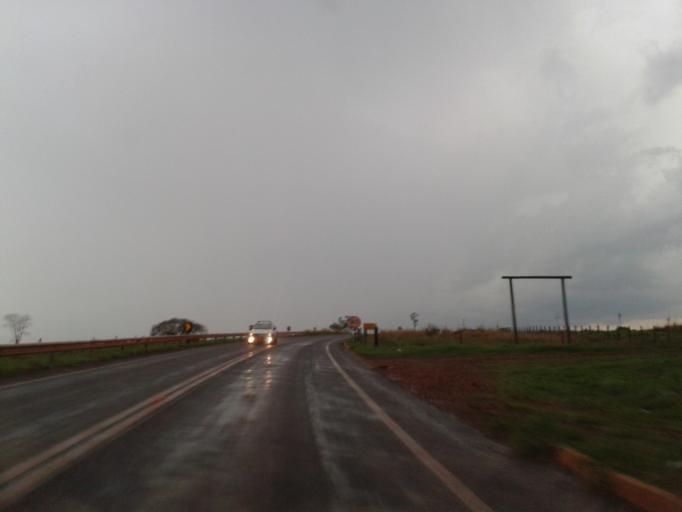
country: BR
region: Goias
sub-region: Quirinopolis
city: Quirinopolis
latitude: -18.4451
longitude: -50.4175
